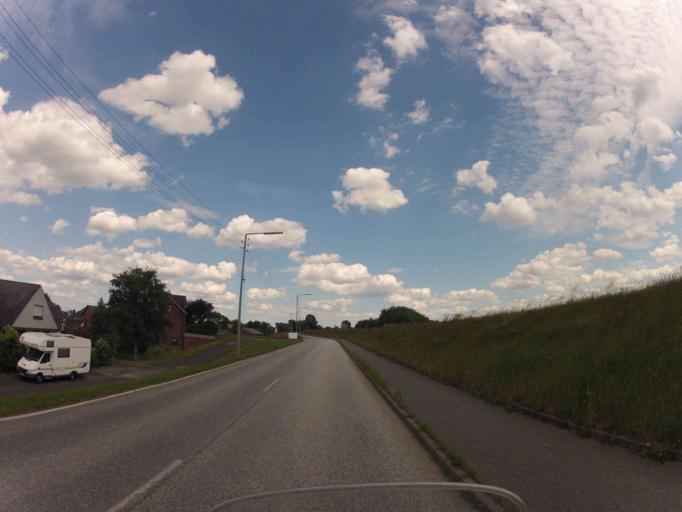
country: DE
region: Lower Saxony
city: Stelle
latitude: 53.4255
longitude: 10.1259
